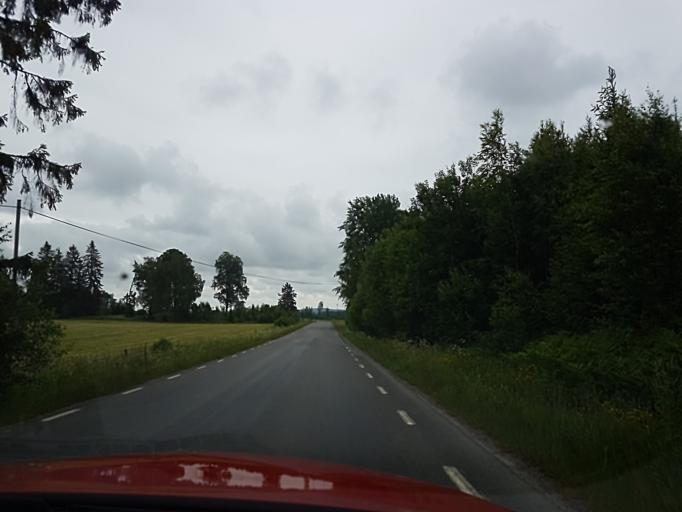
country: SE
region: Vaestra Goetaland
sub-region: Tidaholms Kommun
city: Olofstorp
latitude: 58.3180
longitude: 14.0060
